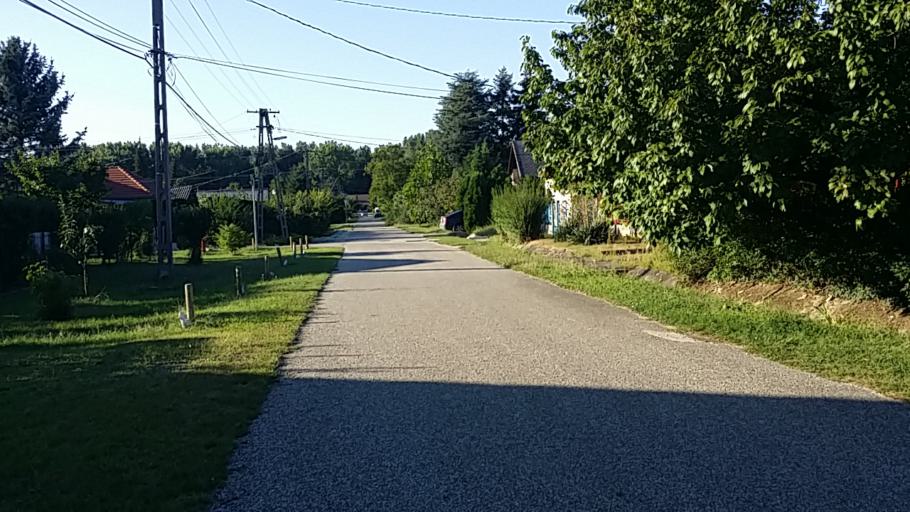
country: HU
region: Gyor-Moson-Sopron
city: Nagycenk
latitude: 47.6185
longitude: 16.7795
